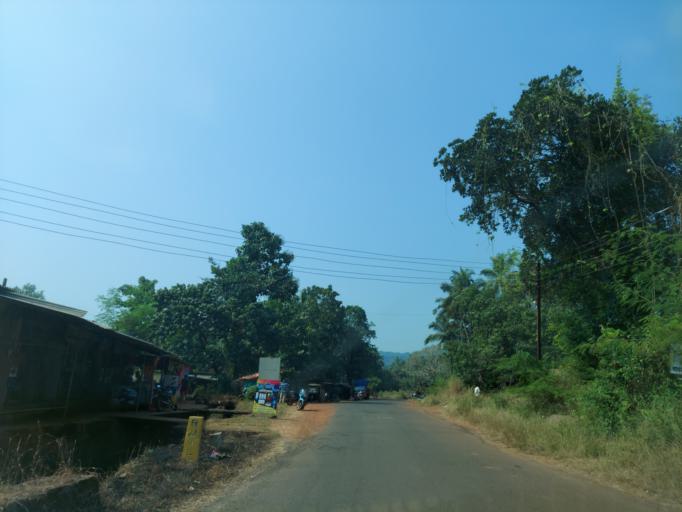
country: IN
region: Maharashtra
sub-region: Sindhudurg
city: Kudal
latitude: 15.9697
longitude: 73.6390
